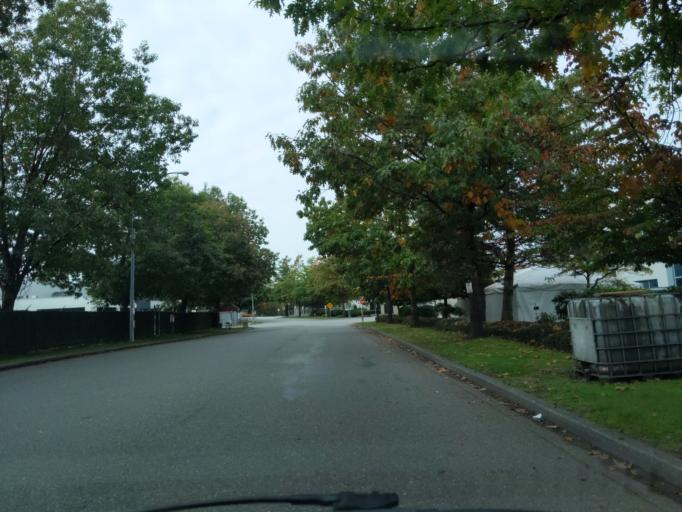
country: CA
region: British Columbia
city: Walnut Grove
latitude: 49.1849
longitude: -122.6620
